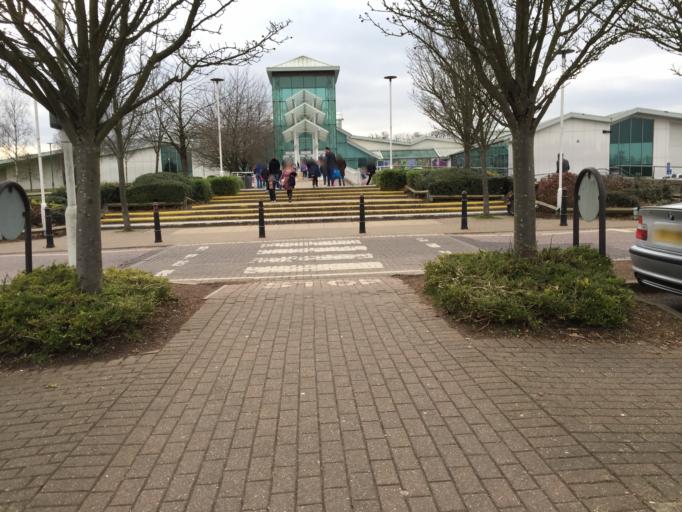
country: GB
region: England
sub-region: Surrey
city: Guildford
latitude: 51.2491
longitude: -0.5610
